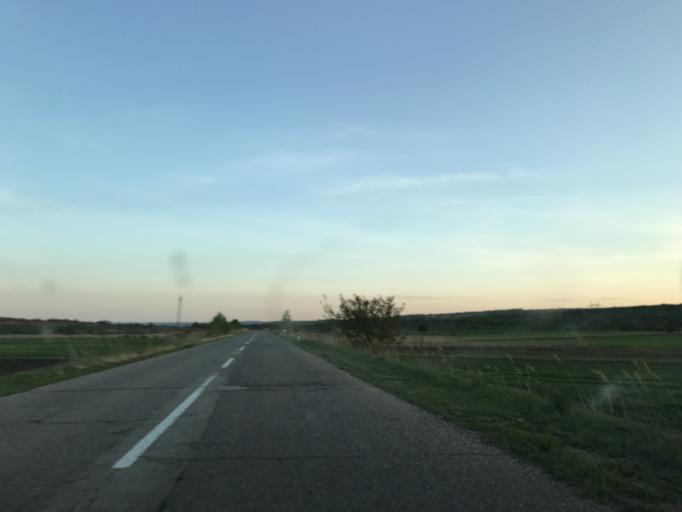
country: RS
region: Central Serbia
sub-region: Borski Okrug
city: Negotin
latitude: 44.2896
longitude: 22.5065
